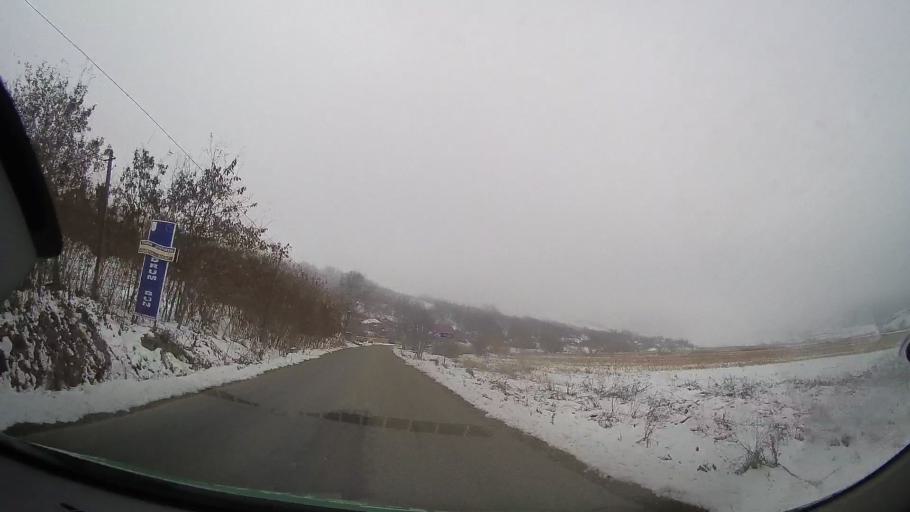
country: RO
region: Bacau
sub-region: Comuna Vultureni
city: Vultureni
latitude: 46.3605
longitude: 27.2876
